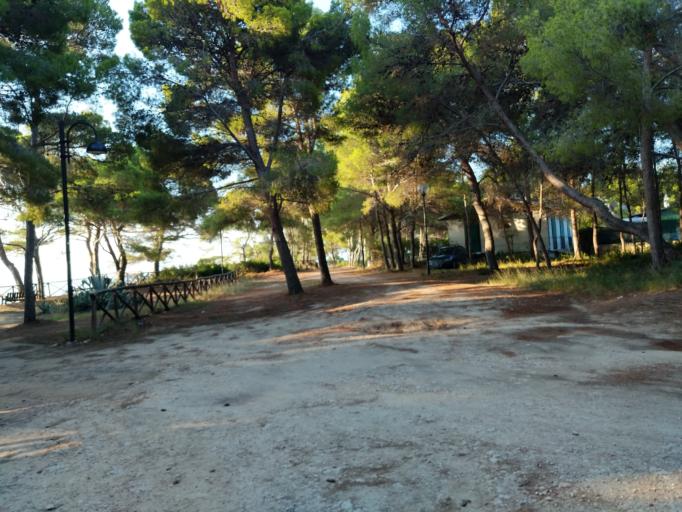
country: IT
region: Apulia
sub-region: Provincia di Foggia
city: Isole Tremiti
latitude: 42.1174
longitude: 15.4931
